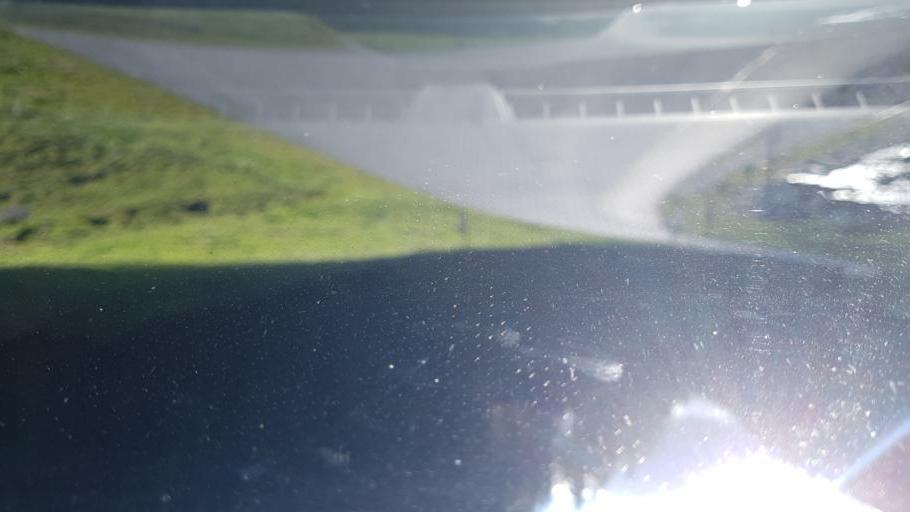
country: AT
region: Styria
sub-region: Politischer Bezirk Liezen
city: Sankt Nikolai im Solktal
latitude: 47.2995
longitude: 14.0709
